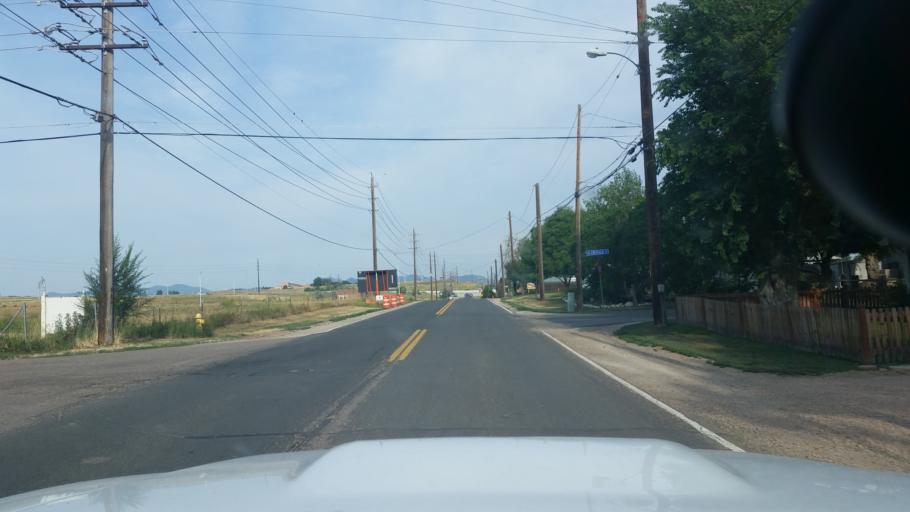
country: US
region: Colorado
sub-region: Broomfield County
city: Broomfield
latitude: 39.9143
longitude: -105.0858
